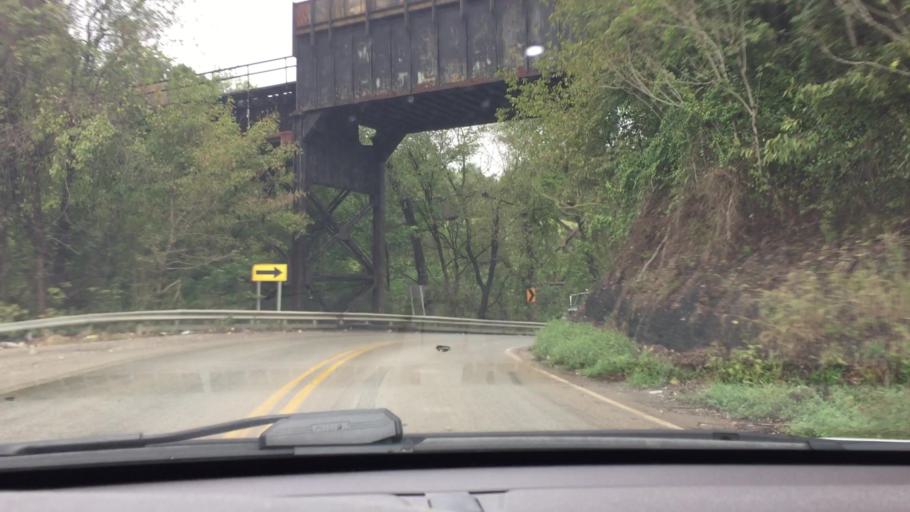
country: US
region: Pennsylvania
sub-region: Westmoreland County
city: Lynnwood-Pricedale
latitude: 40.1416
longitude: -79.8574
